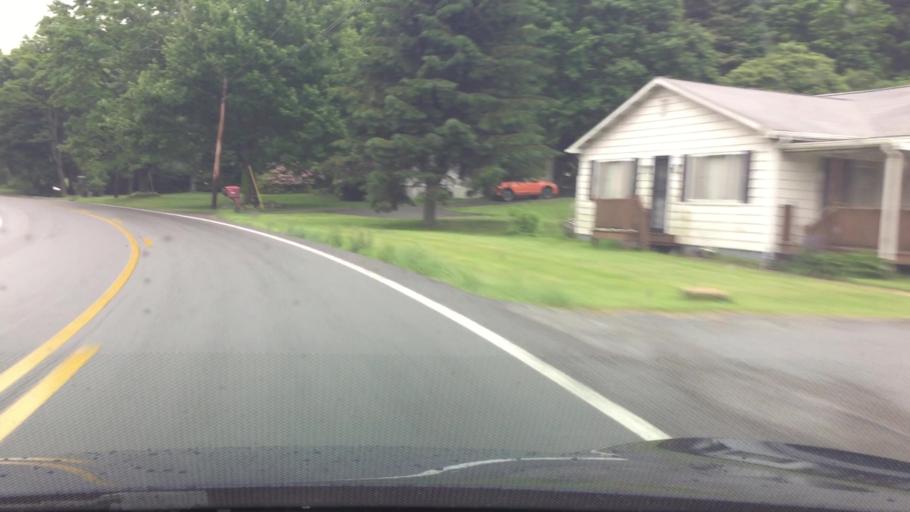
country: US
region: West Virginia
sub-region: Raleigh County
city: Shady Spring
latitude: 37.6923
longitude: -81.0716
